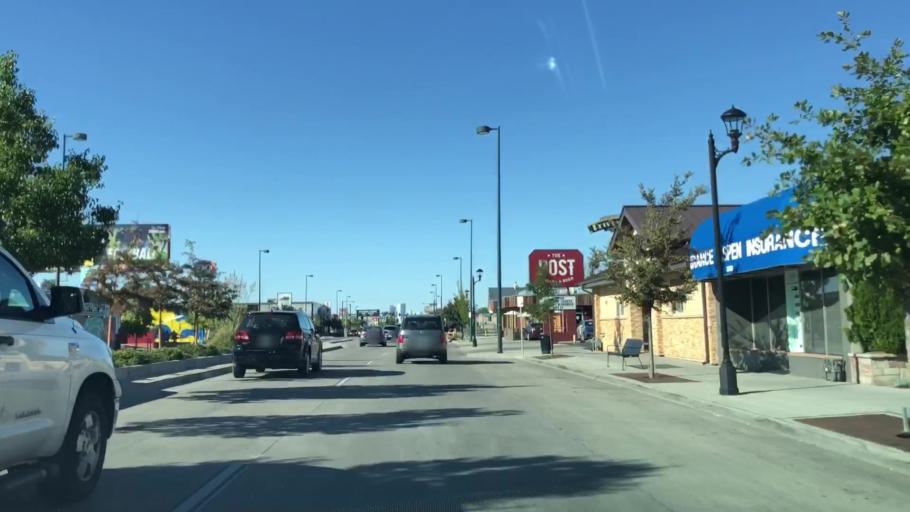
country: US
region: Colorado
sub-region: Arapahoe County
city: Englewood
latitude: 39.6757
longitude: -104.9875
